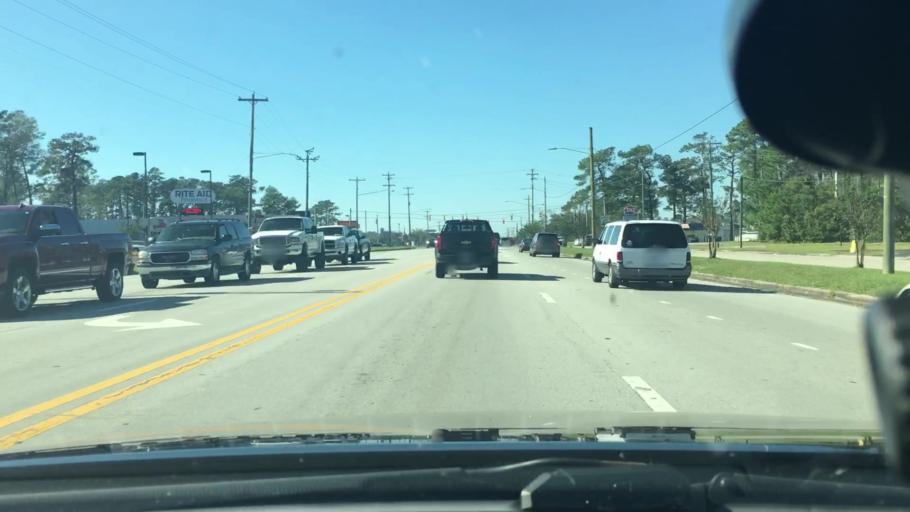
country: US
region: North Carolina
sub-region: Craven County
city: Havelock
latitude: 34.8831
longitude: -76.9109
